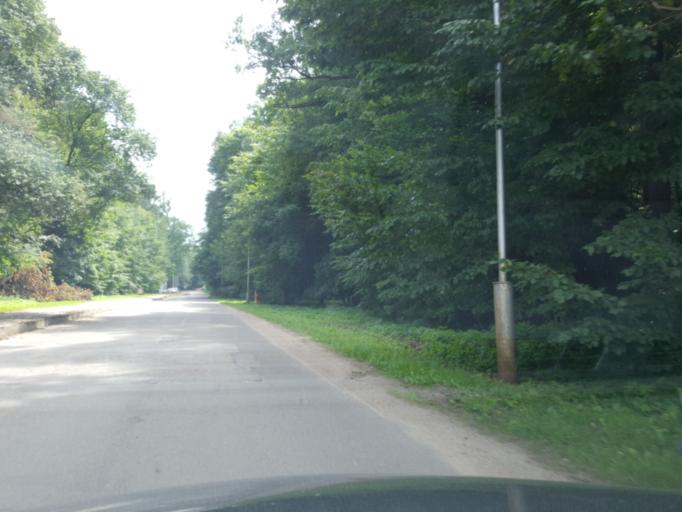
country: LT
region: Alytaus apskritis
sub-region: Alytus
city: Alytus
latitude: 54.3843
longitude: 24.0418
